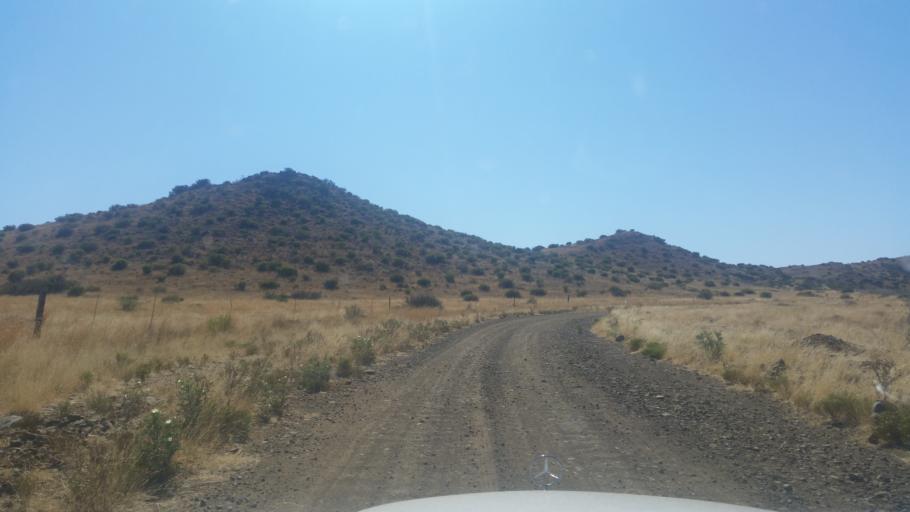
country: ZA
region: Orange Free State
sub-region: Xhariep District Municipality
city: Trompsburg
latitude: -30.4844
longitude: 25.9994
